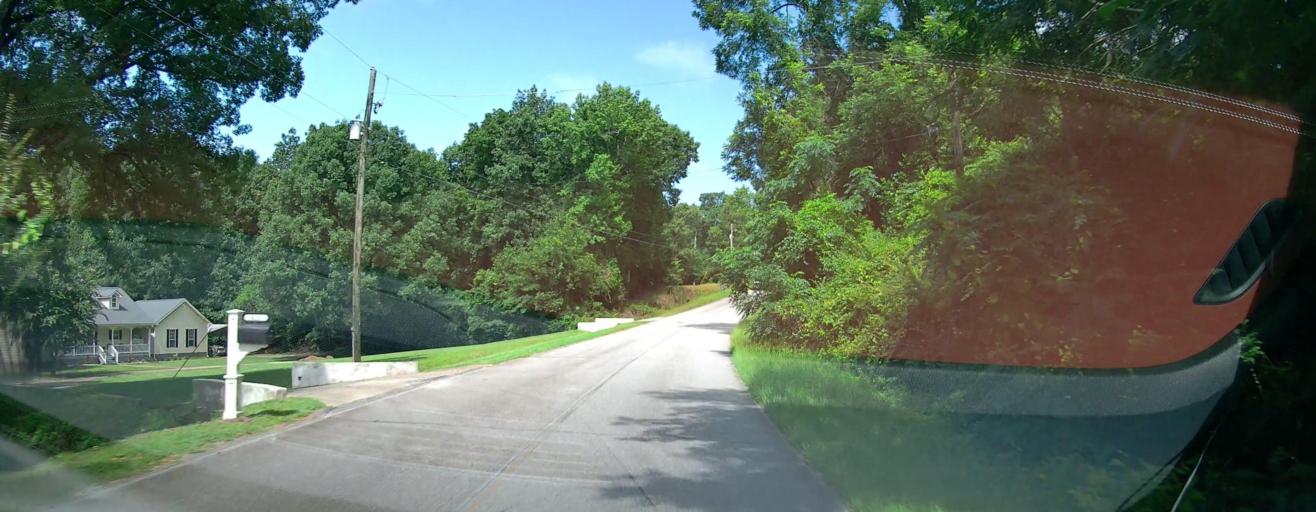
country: US
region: Georgia
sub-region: Peach County
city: Byron
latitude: 32.6607
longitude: -83.7743
